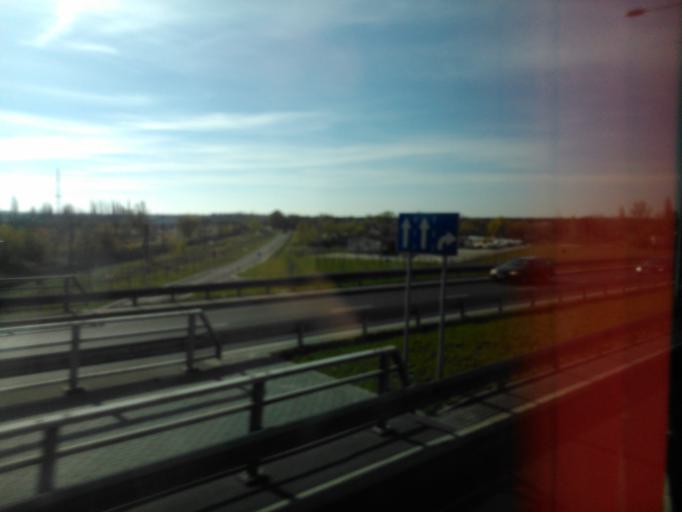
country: PL
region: Kujawsko-Pomorskie
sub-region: Torun
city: Torun
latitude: 52.9970
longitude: 18.6532
